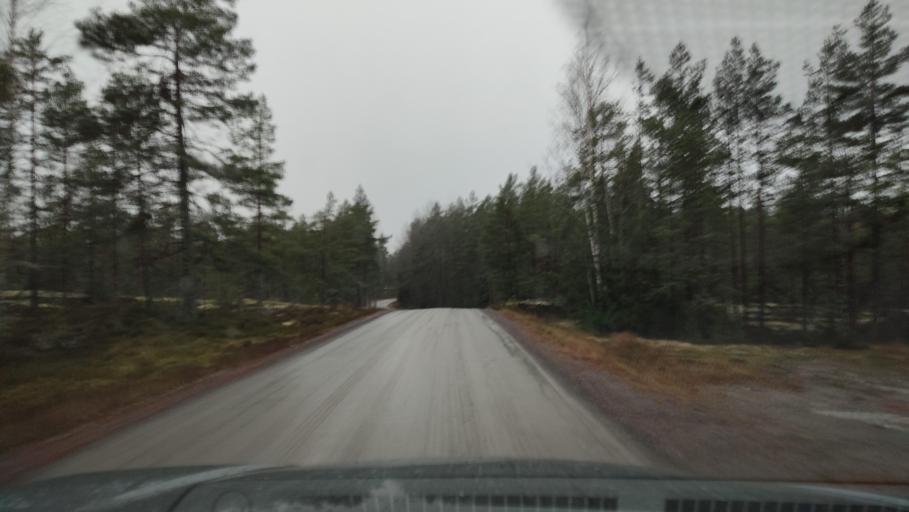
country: FI
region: Southern Ostrobothnia
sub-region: Suupohja
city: Karijoki
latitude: 62.1384
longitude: 21.6541
